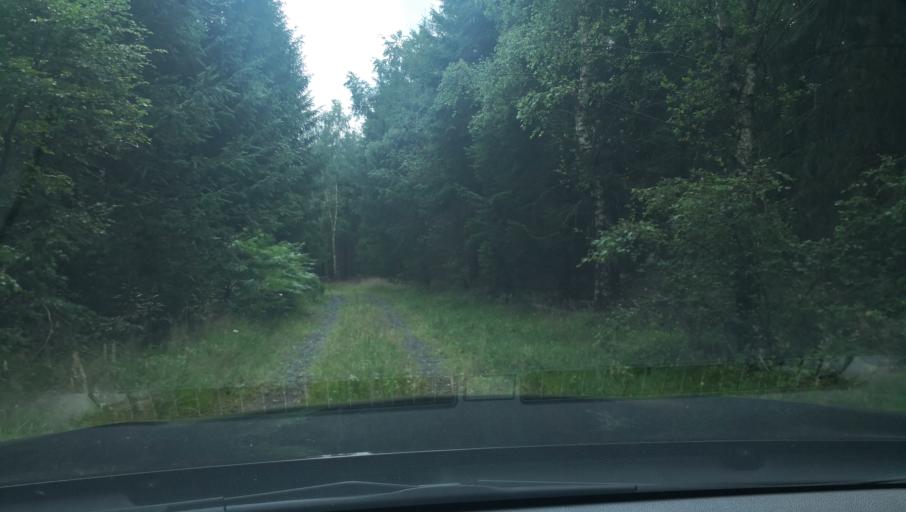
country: SE
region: Skane
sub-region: Simrishamns Kommun
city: Kivik
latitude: 55.6165
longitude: 14.1073
